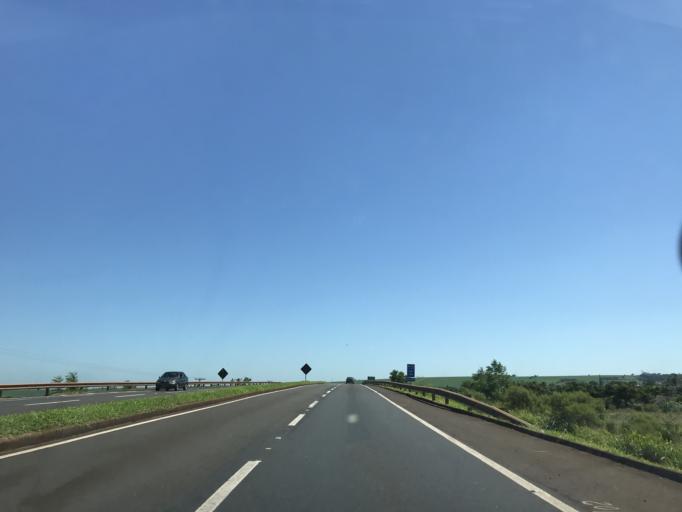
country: BR
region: Parana
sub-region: Marialva
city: Marialva
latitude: -23.4792
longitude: -51.8222
